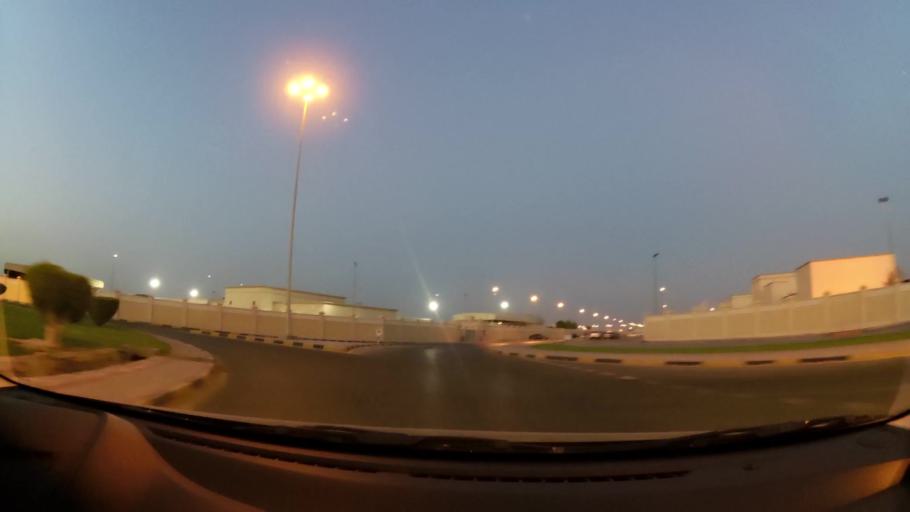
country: OM
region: Muhafazat Masqat
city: As Sib al Jadidah
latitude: 23.6649
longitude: 58.1827
